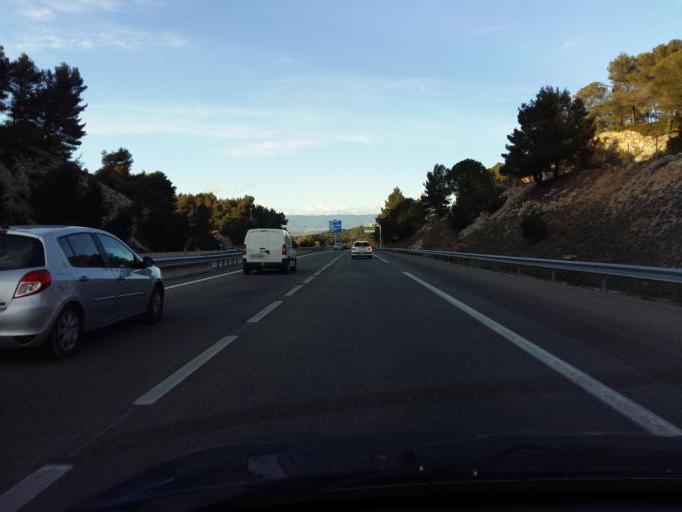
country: FR
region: Provence-Alpes-Cote d'Azur
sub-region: Departement des Bouches-du-Rhone
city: Venelles
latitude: 43.6051
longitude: 5.4972
